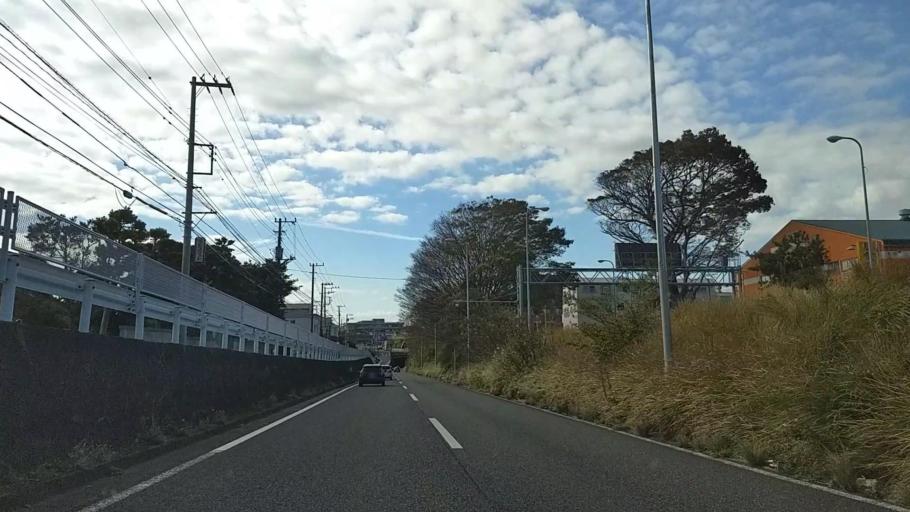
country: JP
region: Kanagawa
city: Fujisawa
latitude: 35.3629
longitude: 139.4964
